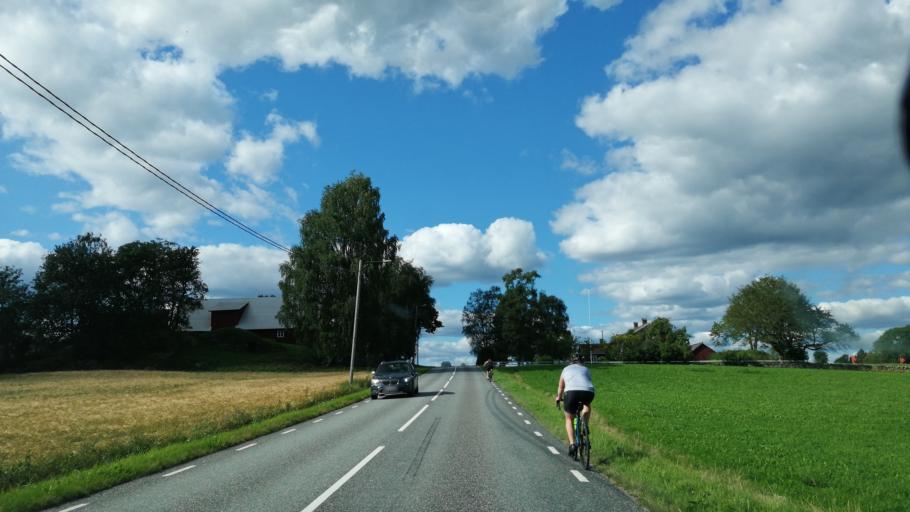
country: SE
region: Joenkoeping
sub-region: Gislaveds Kommun
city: Reftele
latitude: 57.1501
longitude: 13.6324
